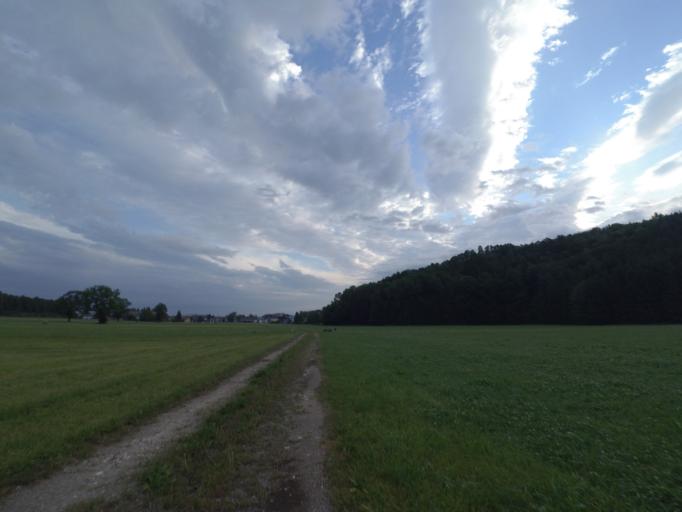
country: AT
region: Salzburg
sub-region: Politischer Bezirk Salzburg-Umgebung
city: Grodig
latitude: 47.7307
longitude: 13.0497
